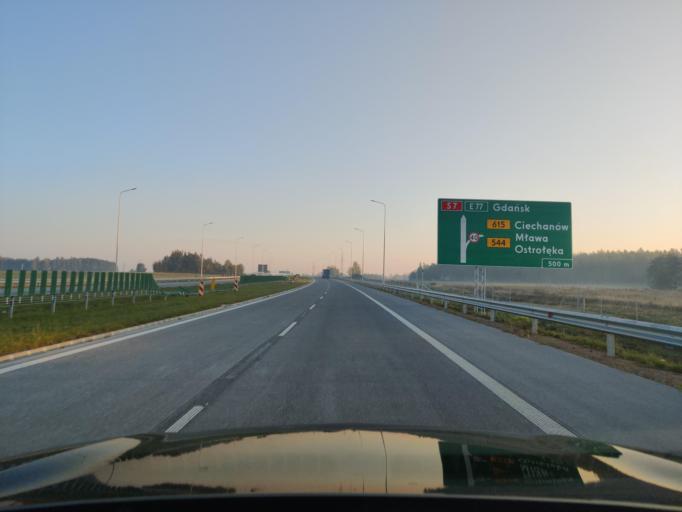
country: PL
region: Masovian Voivodeship
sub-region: Powiat mlawski
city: Mlawa
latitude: 53.0899
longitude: 20.4070
